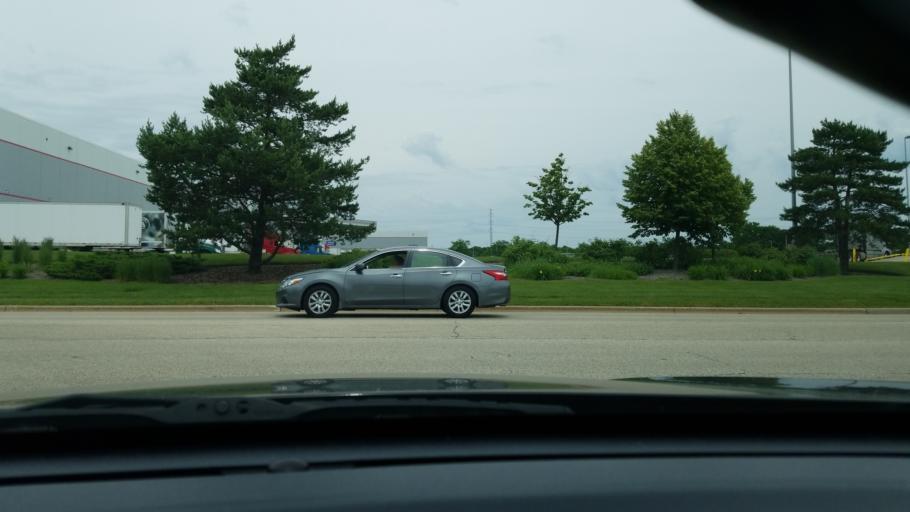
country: US
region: Illinois
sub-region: Kane County
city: Sleepy Hollow
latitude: 42.0730
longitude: -88.3289
